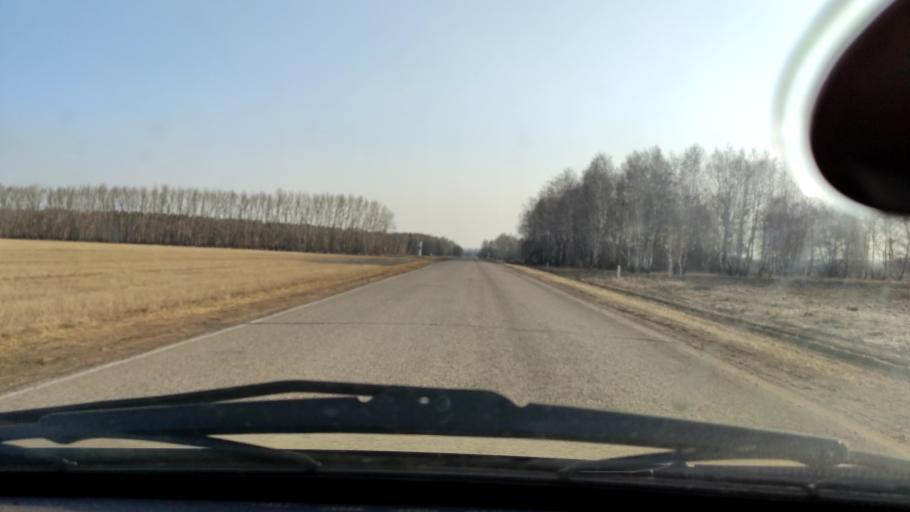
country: RU
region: Bashkortostan
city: Asanovo
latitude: 54.7944
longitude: 55.5256
